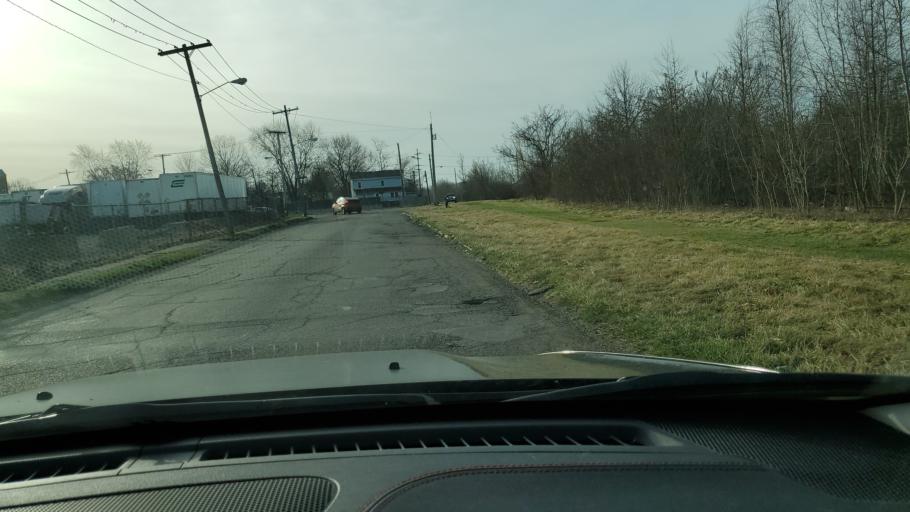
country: US
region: Ohio
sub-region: Trumbull County
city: Niles
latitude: 41.1803
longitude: -80.7561
